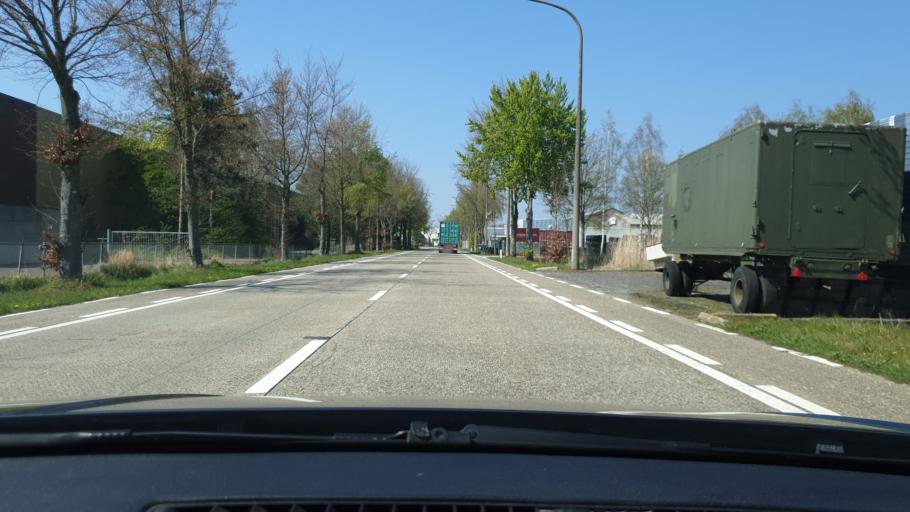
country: BE
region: Flanders
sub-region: Provincie Antwerpen
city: Westerlo
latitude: 51.1250
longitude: 4.9465
